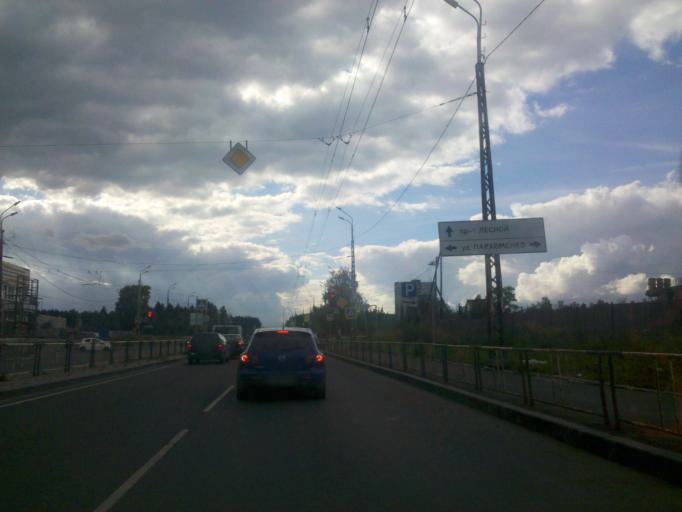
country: RU
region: Republic of Karelia
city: Petrozavodsk
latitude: 61.7823
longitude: 34.3201
